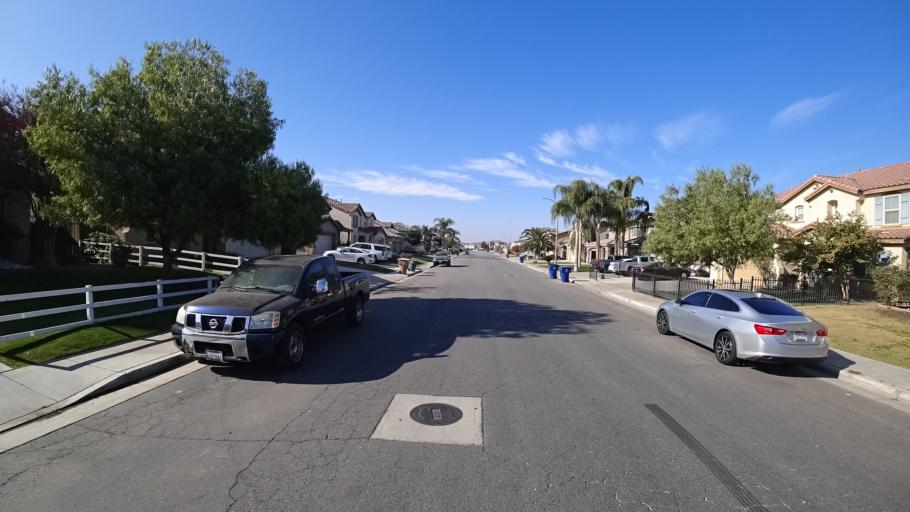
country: US
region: California
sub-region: Kern County
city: Greenfield
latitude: 35.2801
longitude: -119.0636
